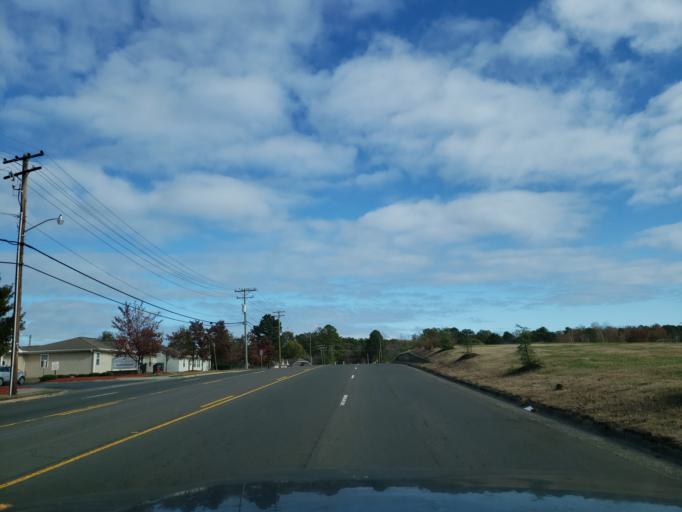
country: US
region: North Carolina
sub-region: Durham County
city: Durham
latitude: 35.9604
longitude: -78.9133
